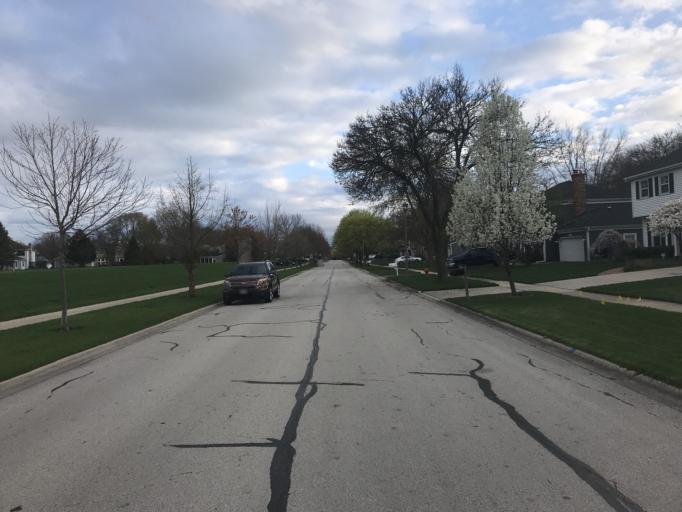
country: US
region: Illinois
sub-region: Will County
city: Bolingbrook
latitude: 41.7356
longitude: -88.1129
